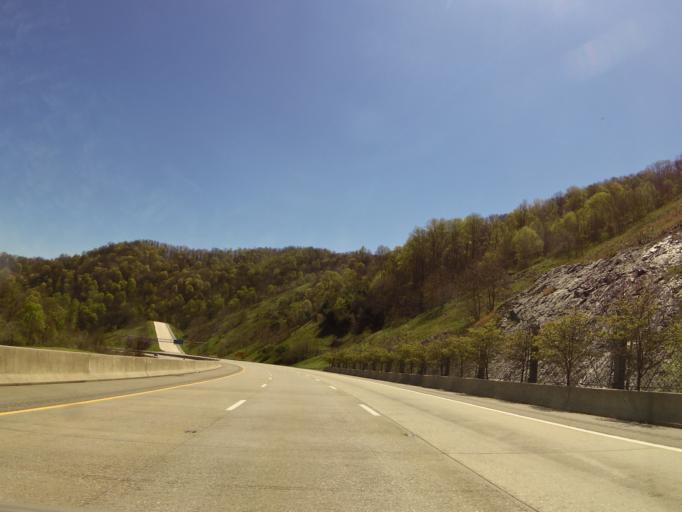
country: US
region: North Carolina
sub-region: Madison County
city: Mars Hill
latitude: 35.8854
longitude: -82.5491
